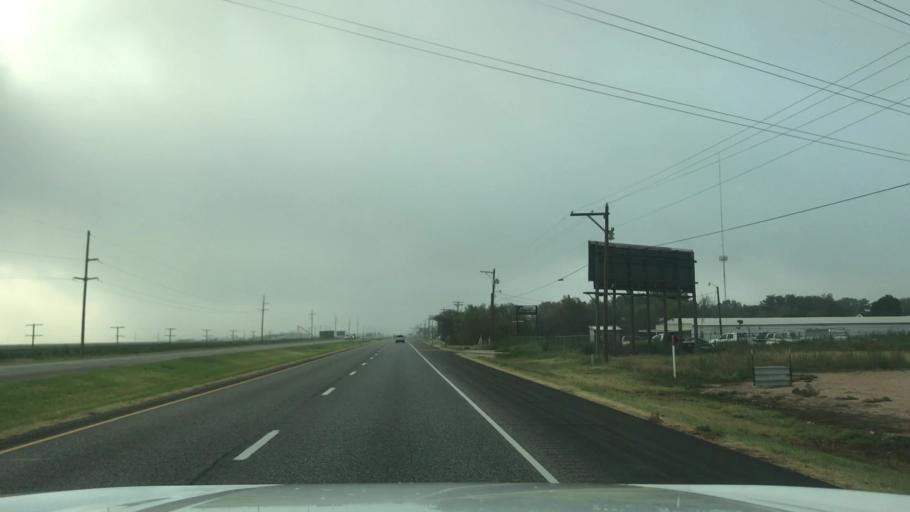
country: US
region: Texas
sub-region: Lubbock County
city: Ransom Canyon
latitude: 33.4972
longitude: -101.7370
